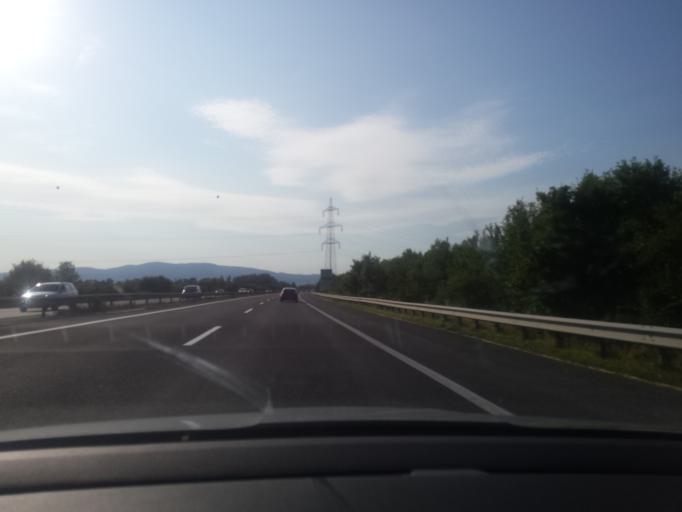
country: AT
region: Lower Austria
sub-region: Politischer Bezirk Modling
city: Munchendorf
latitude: 48.0096
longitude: 16.3735
